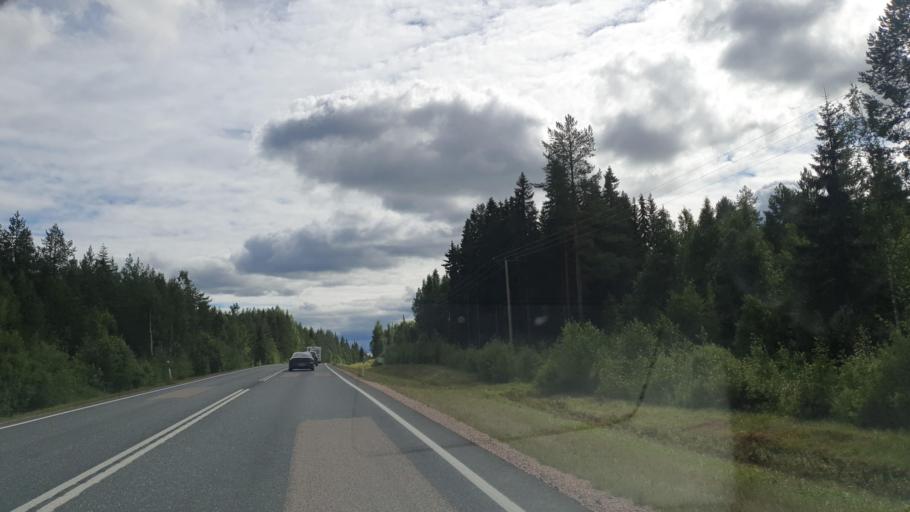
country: FI
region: Kainuu
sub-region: Kajaani
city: Kajaani
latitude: 64.0938
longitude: 27.4517
